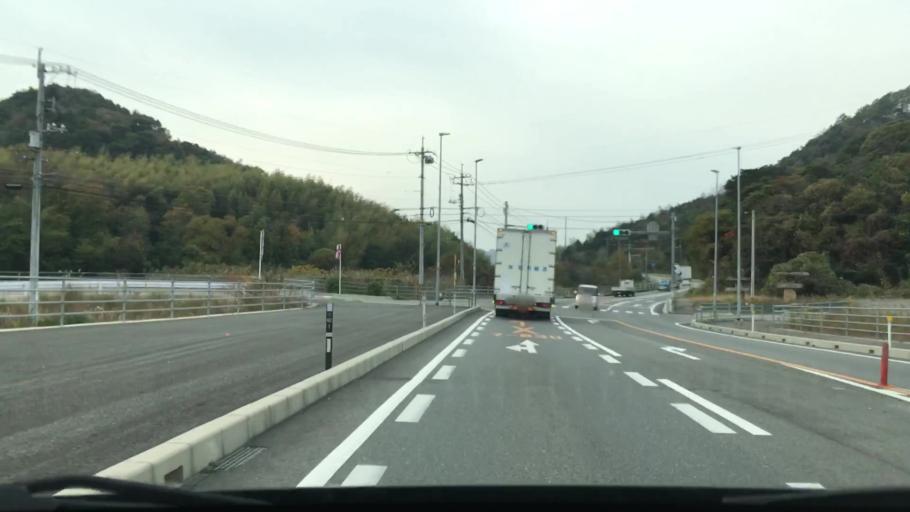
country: JP
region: Yamaguchi
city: Hofu
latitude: 34.0647
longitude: 131.4822
